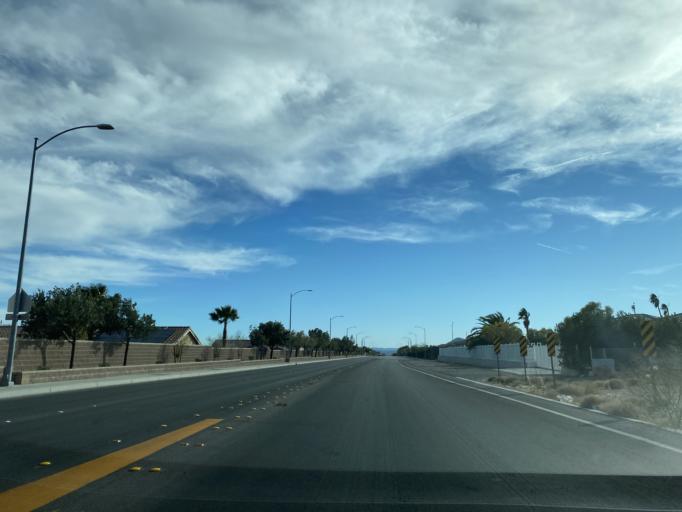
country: US
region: Nevada
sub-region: Clark County
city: Summerlin South
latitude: 36.2950
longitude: -115.3059
